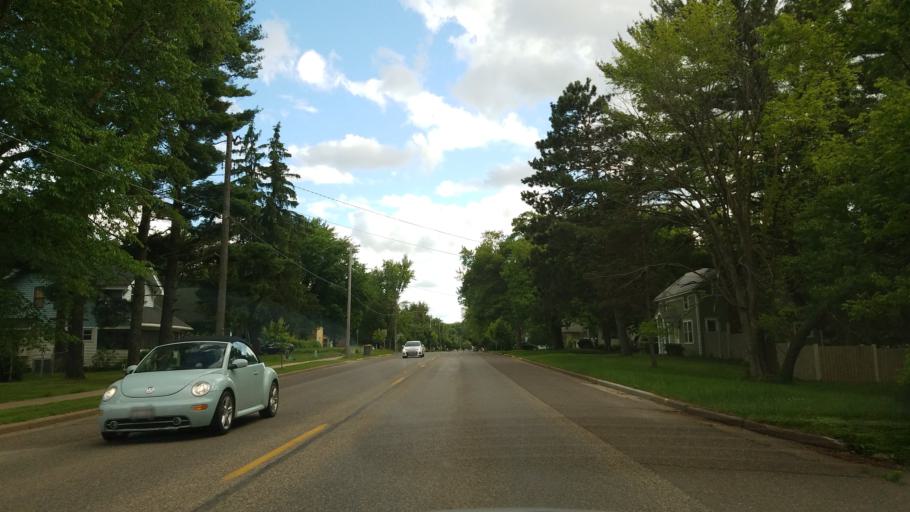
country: US
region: Wisconsin
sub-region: Polk County
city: Osceola
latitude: 45.3275
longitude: -92.6993
